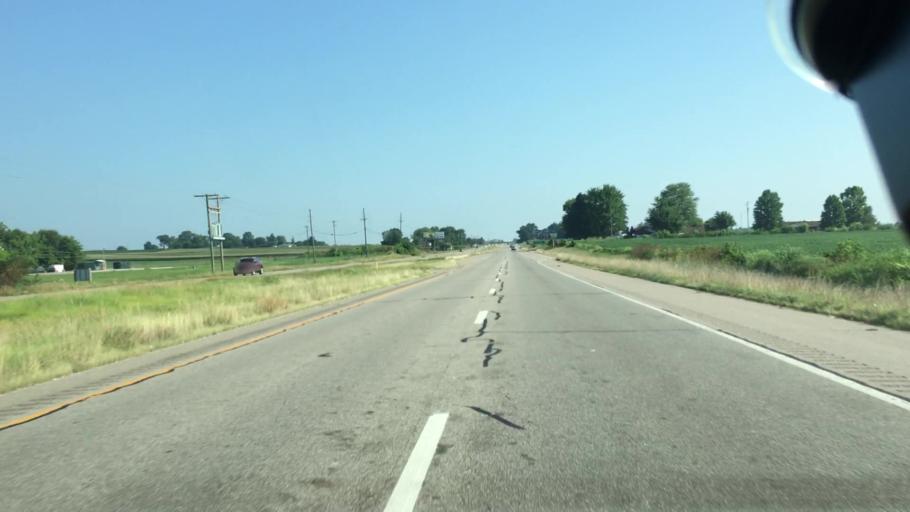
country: US
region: Indiana
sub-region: Gibson County
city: Fort Branch
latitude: 38.2571
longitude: -87.5678
